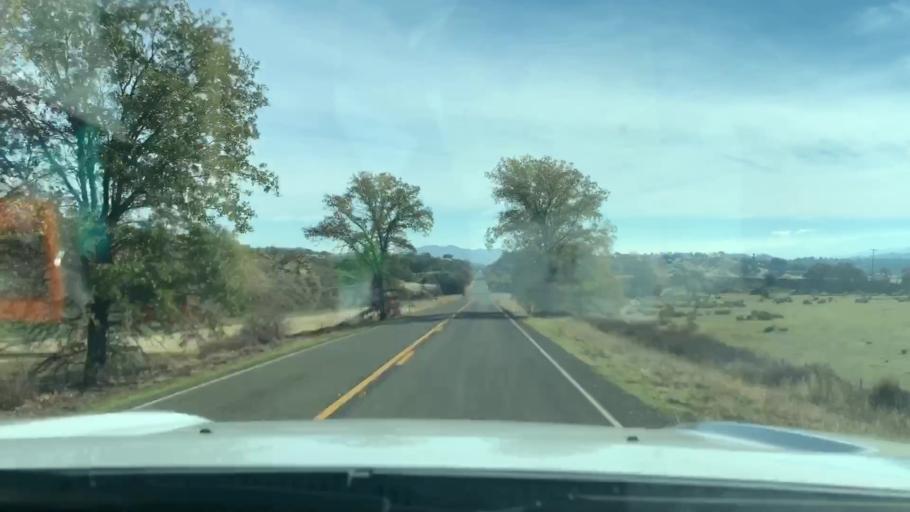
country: US
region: California
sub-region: Fresno County
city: Coalinga
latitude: 36.1024
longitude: -120.5490
